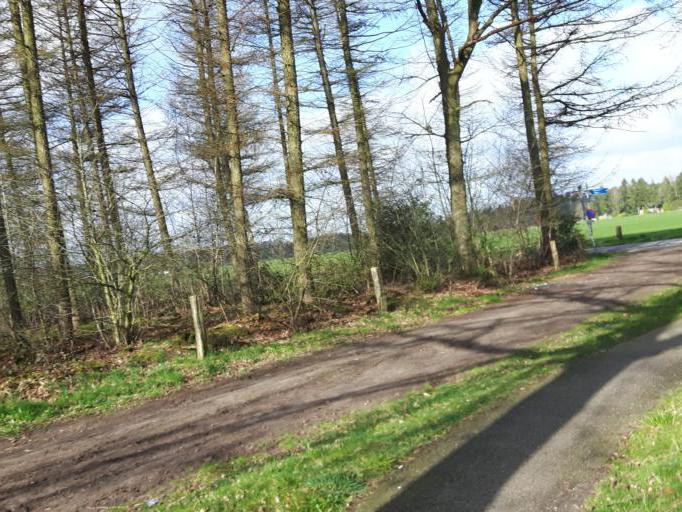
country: NL
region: Overijssel
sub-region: Gemeente Enschede
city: Enschede
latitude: 52.1856
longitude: 6.8321
